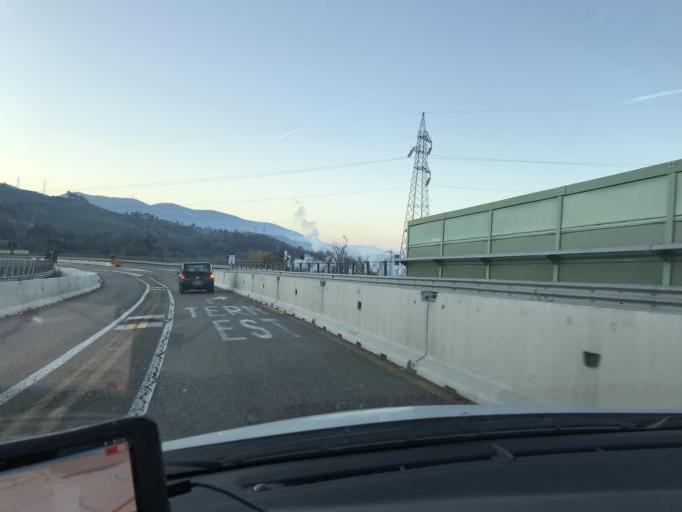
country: IT
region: Umbria
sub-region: Provincia di Terni
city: Terni
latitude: 42.5786
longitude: 12.6805
